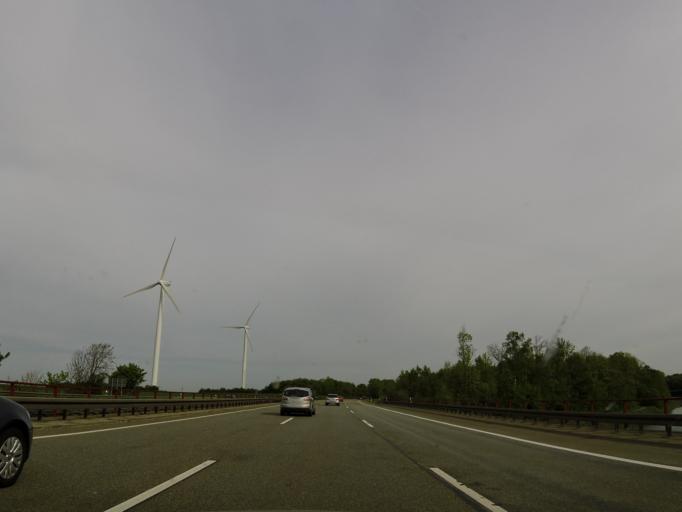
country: DE
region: Lower Saxony
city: Harsum
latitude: 52.2005
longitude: 9.9409
